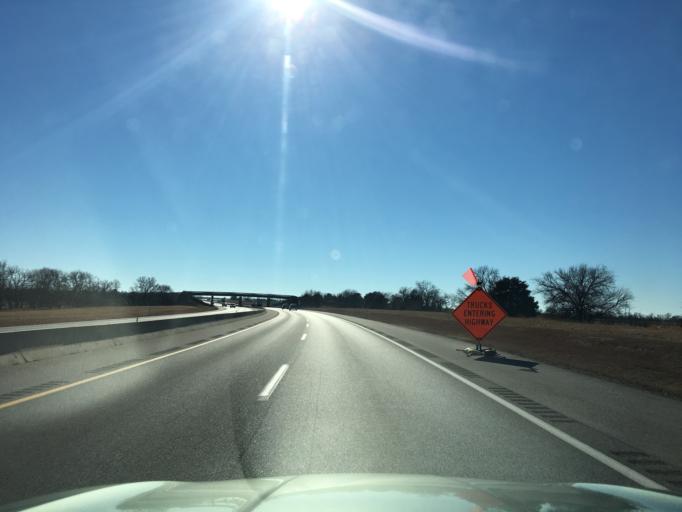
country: US
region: Kansas
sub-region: Sumner County
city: Wellington
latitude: 37.1919
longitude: -97.3419
